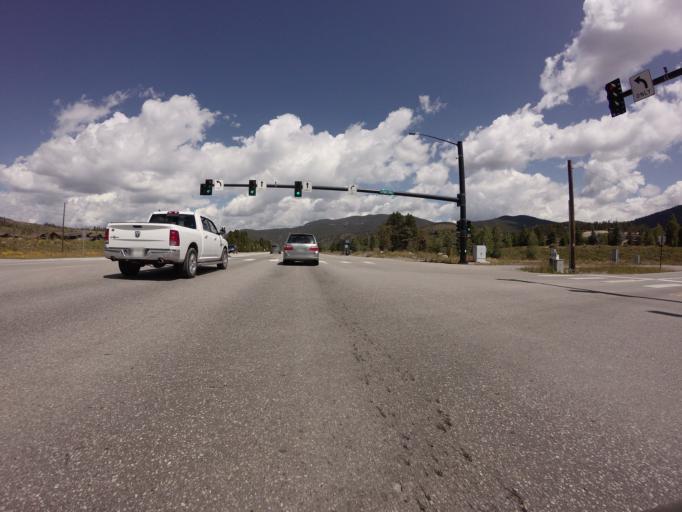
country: US
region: Colorado
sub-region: Summit County
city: Breckenridge
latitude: 39.5322
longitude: -106.0438
